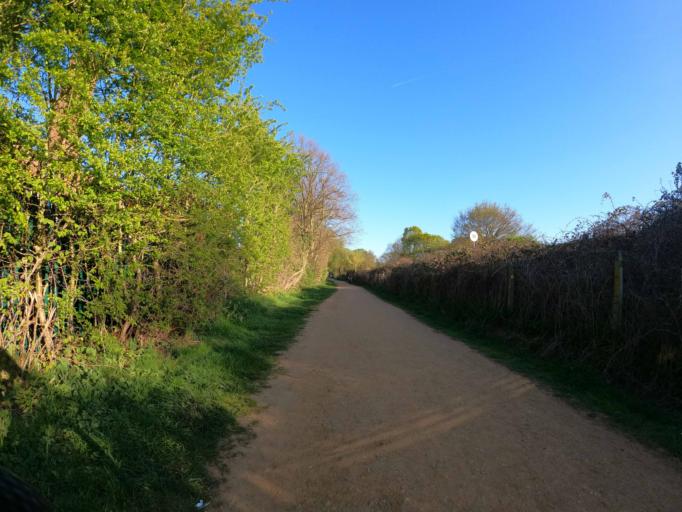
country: GB
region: England
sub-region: Greater London
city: Isleworth
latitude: 51.5007
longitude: -0.3414
